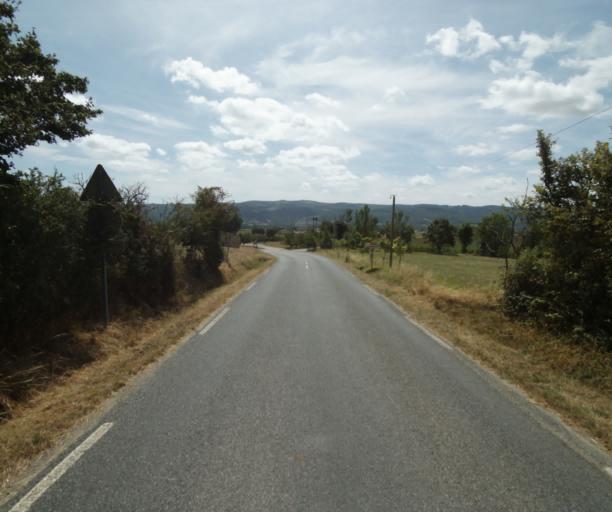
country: FR
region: Midi-Pyrenees
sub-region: Departement du Tarn
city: Dourgne
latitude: 43.5034
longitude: 2.0951
